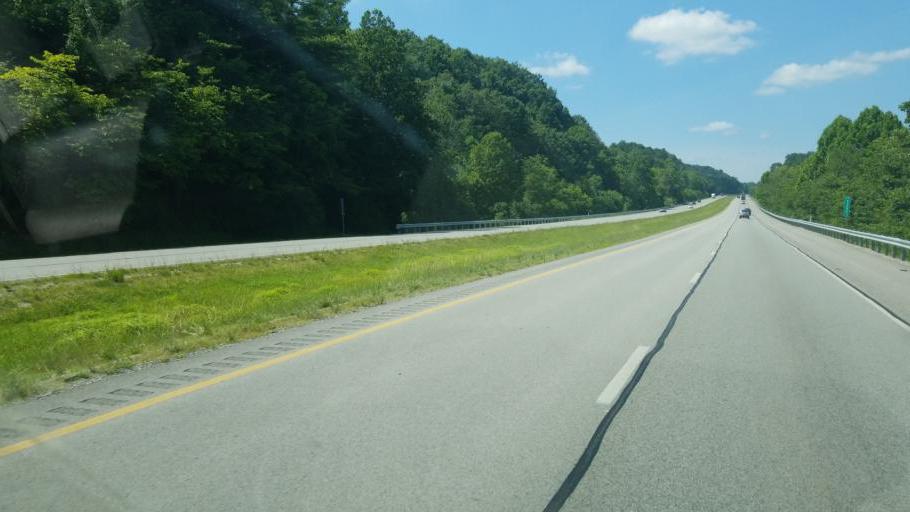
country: US
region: West Virginia
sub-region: Kanawha County
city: Sissonville
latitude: 38.6329
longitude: -81.6483
